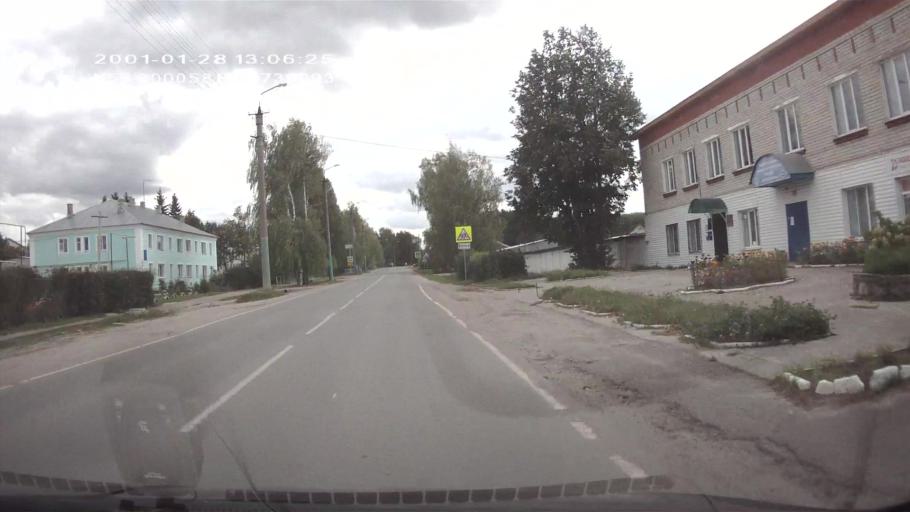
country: RU
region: Mariy-El
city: Kuzhener
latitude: 56.9998
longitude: 48.7394
